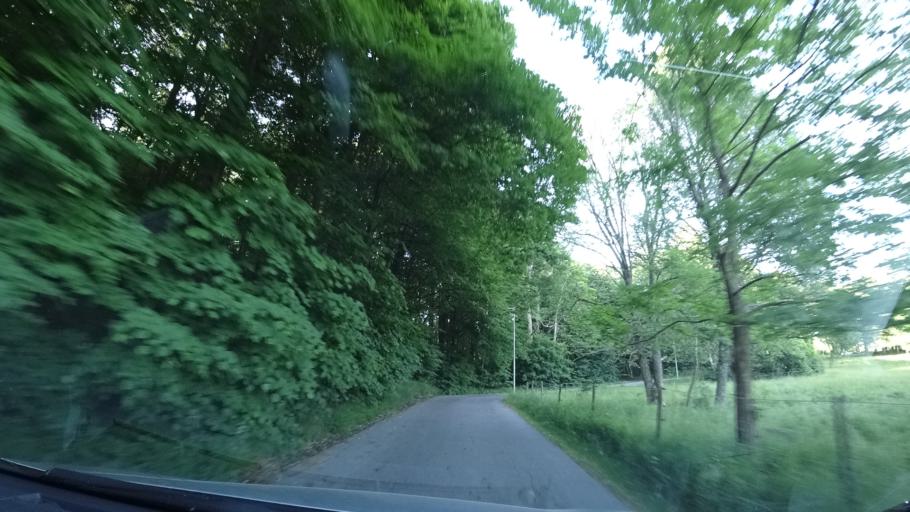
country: SE
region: Vaestra Goetaland
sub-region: Goteborg
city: Billdal
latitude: 57.5829
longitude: 11.9857
